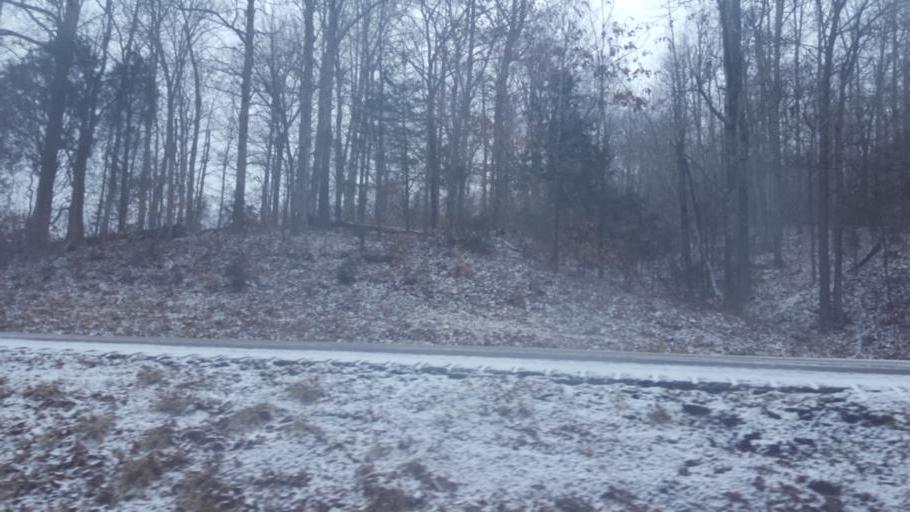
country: US
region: Kentucky
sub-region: Crittenden County
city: Marion
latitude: 37.4477
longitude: -88.0578
